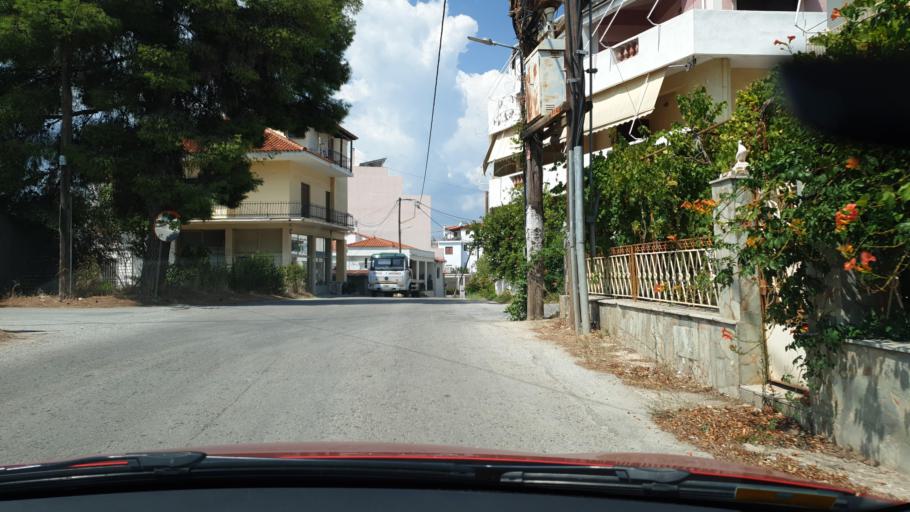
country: GR
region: Central Greece
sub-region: Nomos Evvoias
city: Aliveri
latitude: 38.4046
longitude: 24.0456
